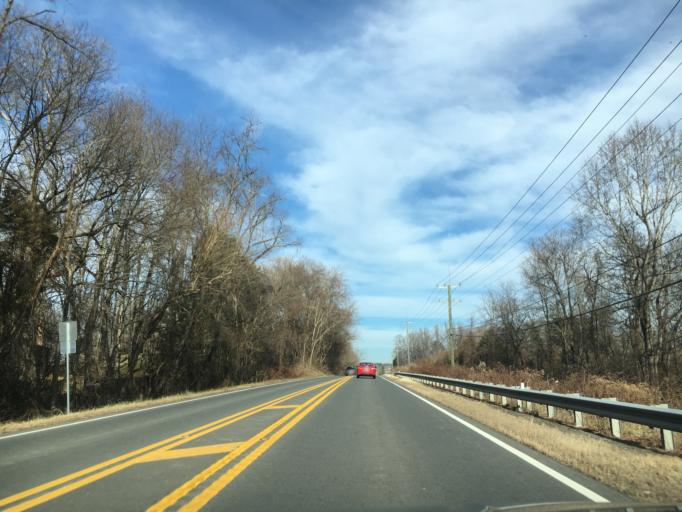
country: US
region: Virginia
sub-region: Fauquier County
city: Warrenton
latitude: 38.6627
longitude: -77.9234
